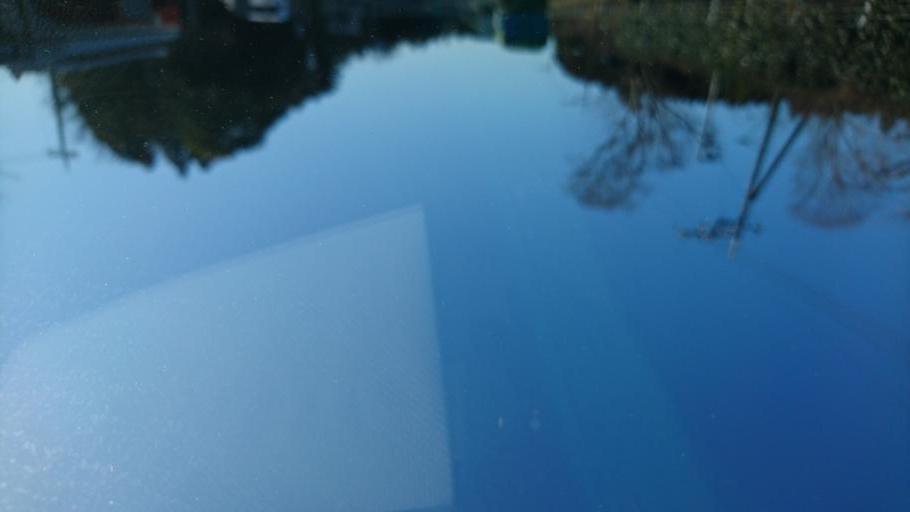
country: JP
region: Chiba
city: Oami
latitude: 35.5689
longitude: 140.2465
